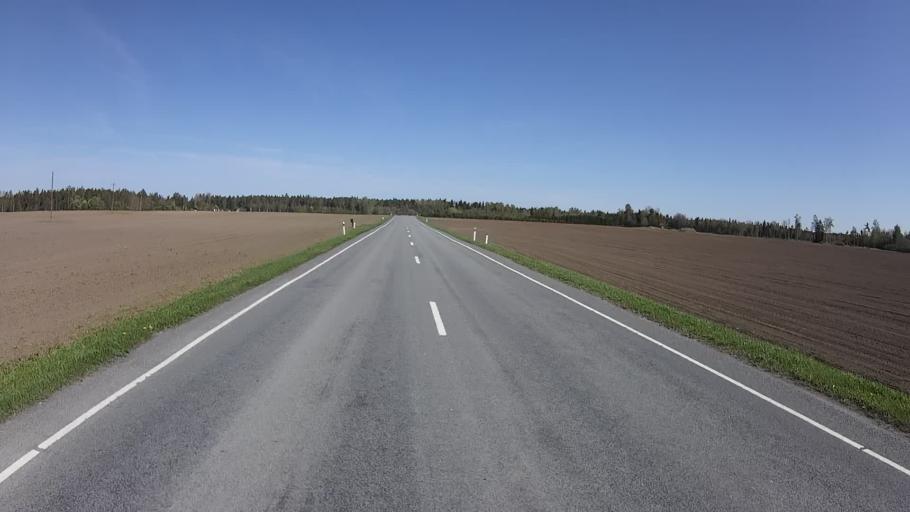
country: EE
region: Raplamaa
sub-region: Jaervakandi vald
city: Jarvakandi
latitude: 58.8434
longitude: 24.7963
